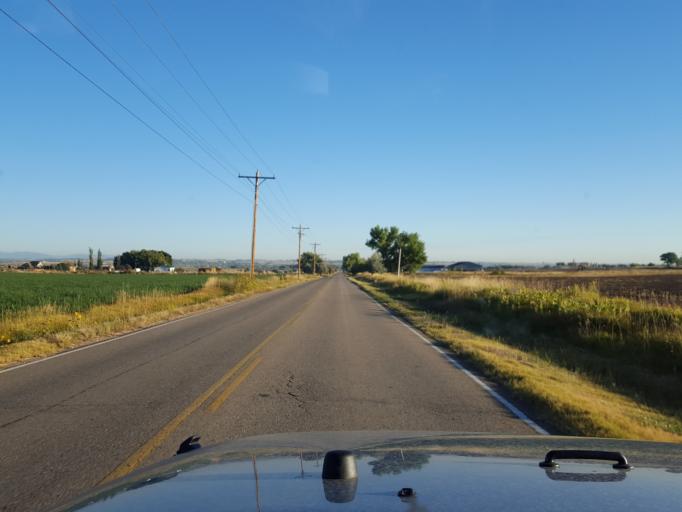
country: US
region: Colorado
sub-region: Weld County
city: Firestone
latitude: 40.1108
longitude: -104.9988
